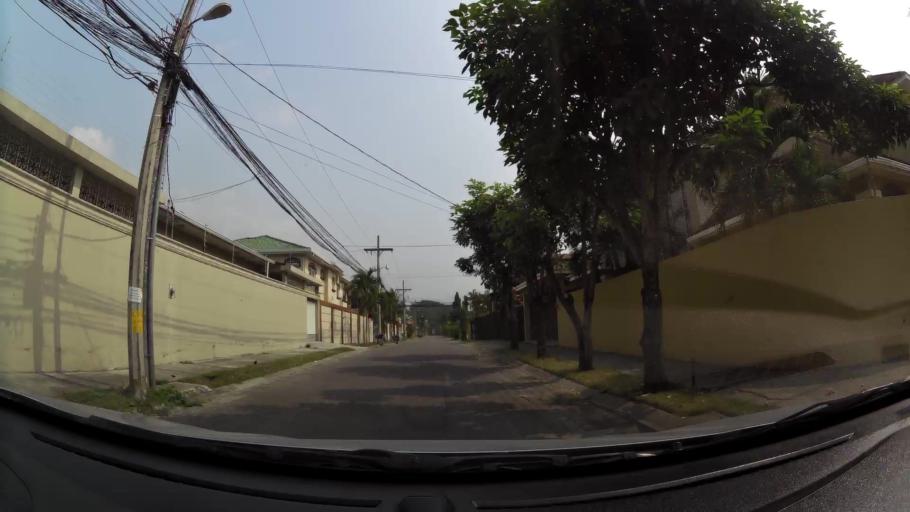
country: HN
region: Cortes
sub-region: San Pedro Sula
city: Pena Blanca
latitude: 15.5355
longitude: -88.0310
